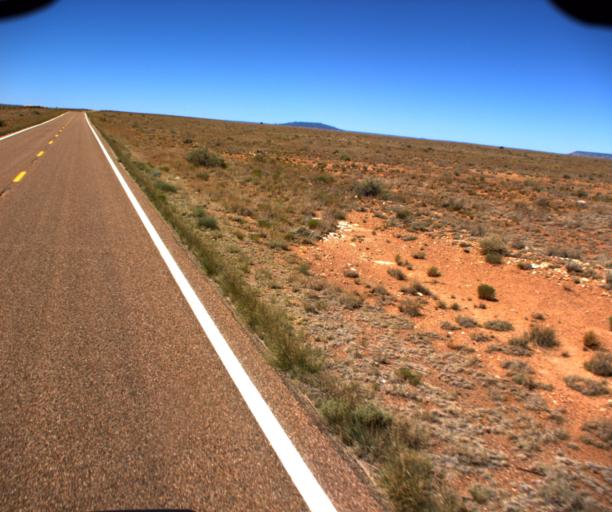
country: US
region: Arizona
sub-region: Navajo County
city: Winslow
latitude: 34.8720
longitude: -110.6561
